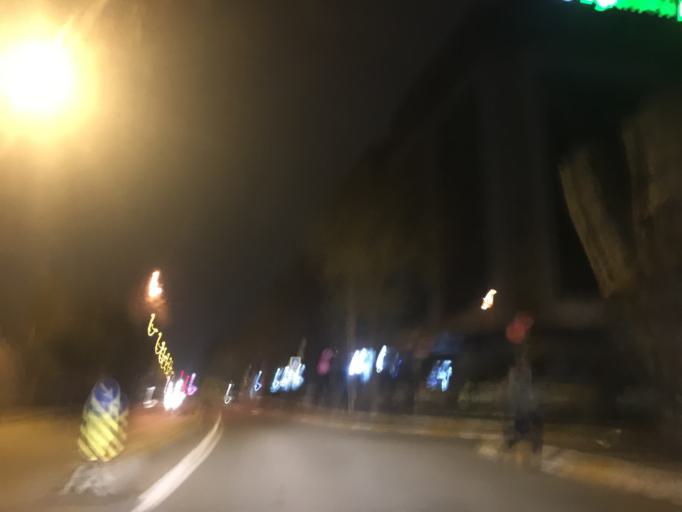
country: TR
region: Istanbul
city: Icmeler
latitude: 40.8218
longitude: 29.3093
